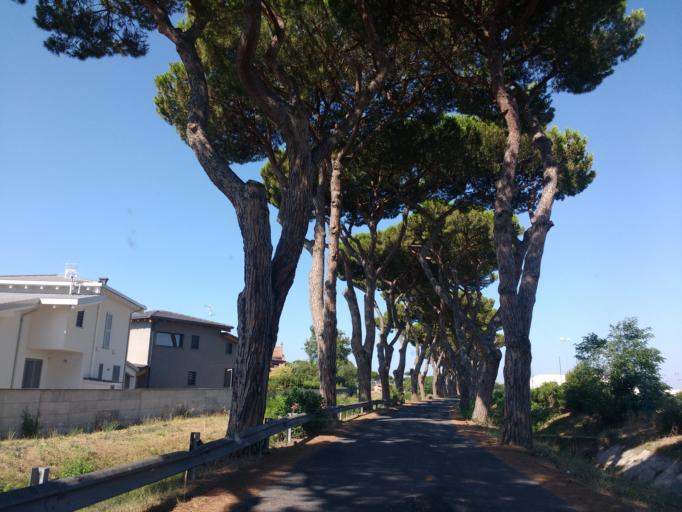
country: IT
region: Latium
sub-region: Citta metropolitana di Roma Capitale
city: Acilia-Castel Fusano-Ostia Antica
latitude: 41.7522
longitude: 12.3347
